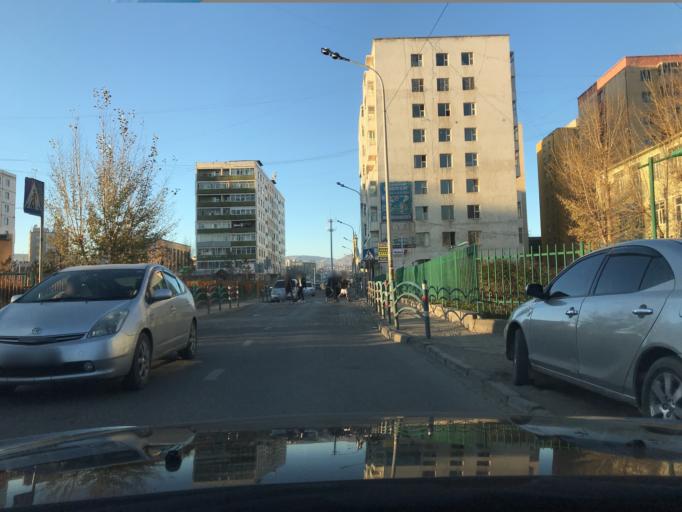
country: MN
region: Ulaanbaatar
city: Ulaanbaatar
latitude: 47.9261
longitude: 106.9057
